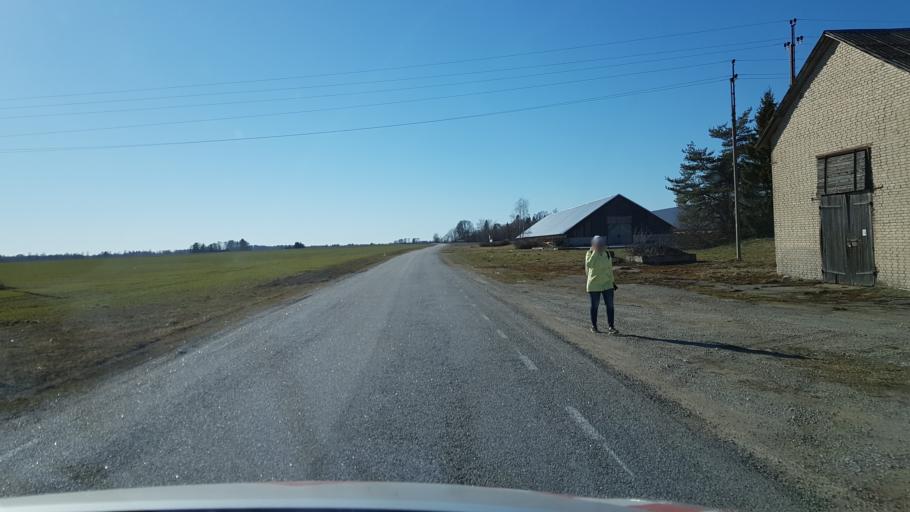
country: EE
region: Laeaene-Virumaa
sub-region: Haljala vald
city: Haljala
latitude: 59.4332
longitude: 26.2397
